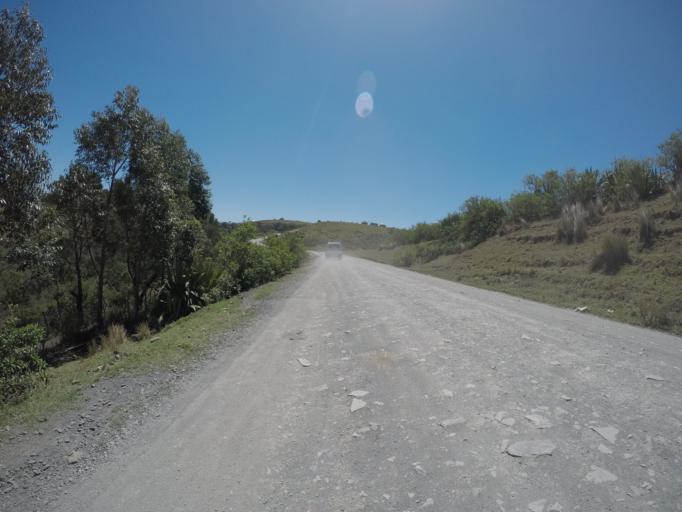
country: ZA
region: Eastern Cape
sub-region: OR Tambo District Municipality
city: Libode
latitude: -31.9909
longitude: 29.0538
